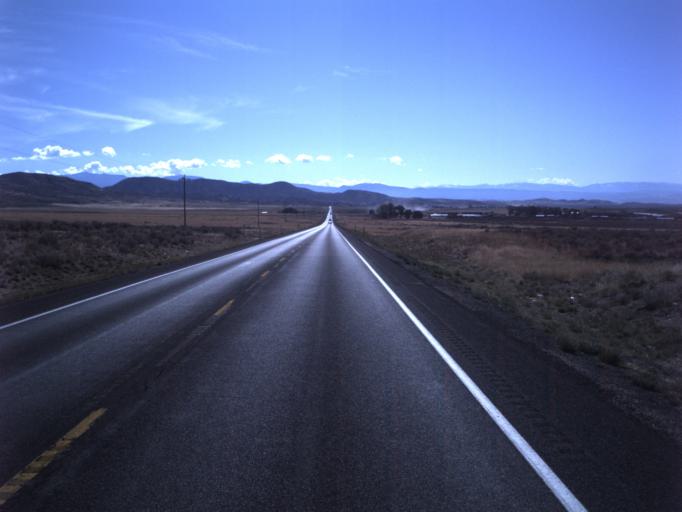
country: US
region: Utah
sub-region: Sanpete County
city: Gunnison
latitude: 39.2768
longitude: -111.8767
